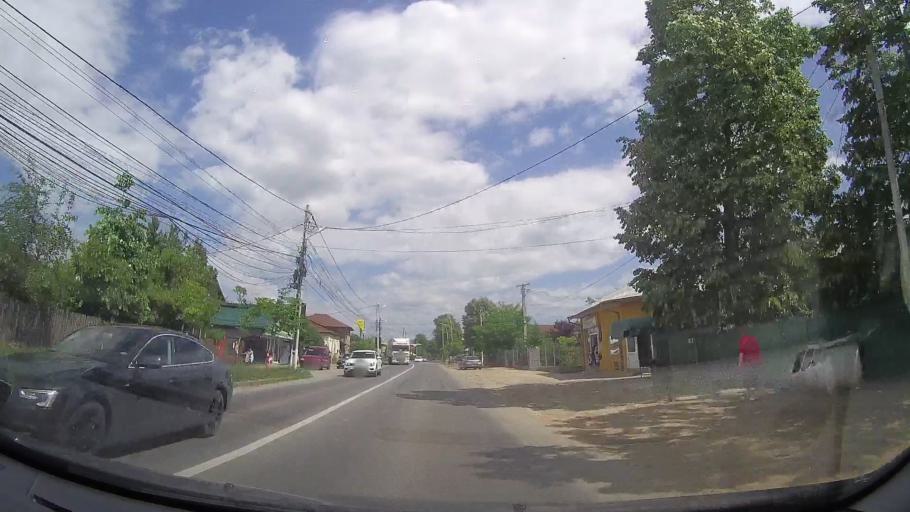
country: RO
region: Prahova
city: Drajna de Jos
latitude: 45.1990
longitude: 26.0437
